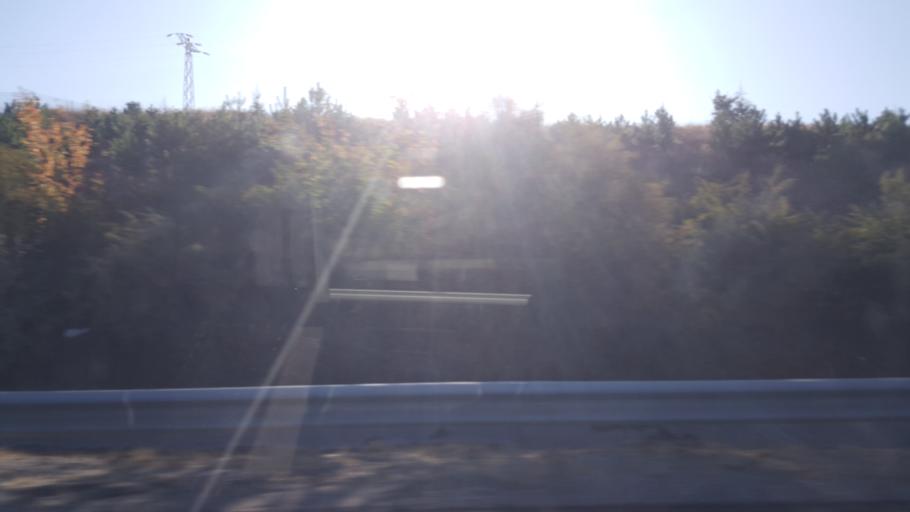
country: TR
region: Ankara
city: Cankaya
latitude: 39.8348
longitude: 32.8891
